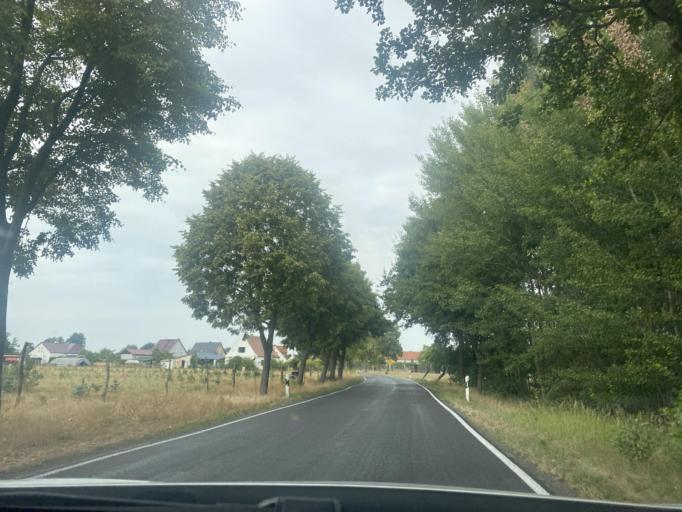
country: DE
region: Saxony
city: Wittichenau
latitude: 51.3515
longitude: 14.2838
